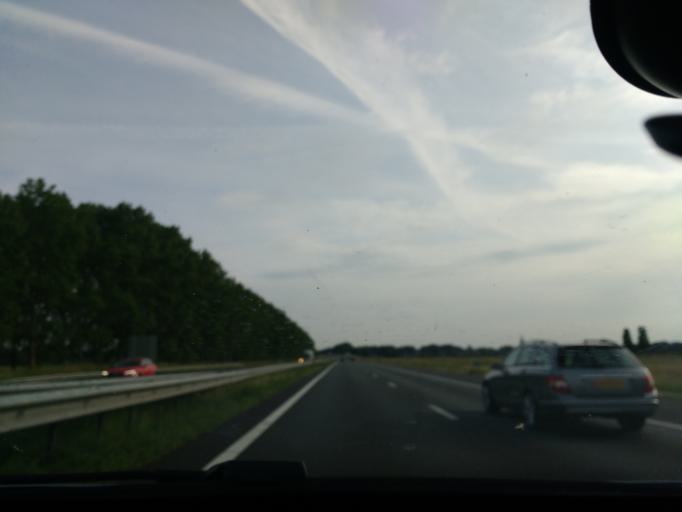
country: NL
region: Gelderland
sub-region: Gemeente Wijchen
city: Bergharen
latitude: 51.8418
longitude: 5.6934
